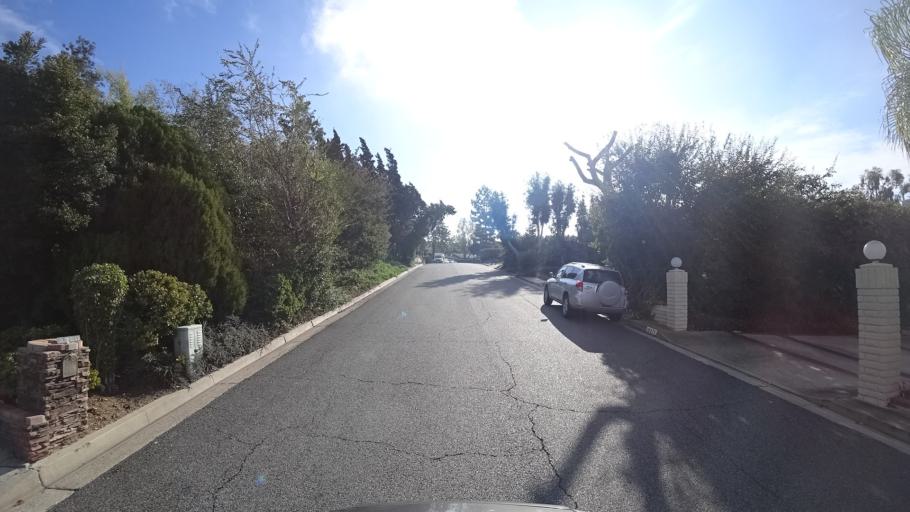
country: US
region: California
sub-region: Orange County
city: North Tustin
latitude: 33.7751
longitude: -117.7743
